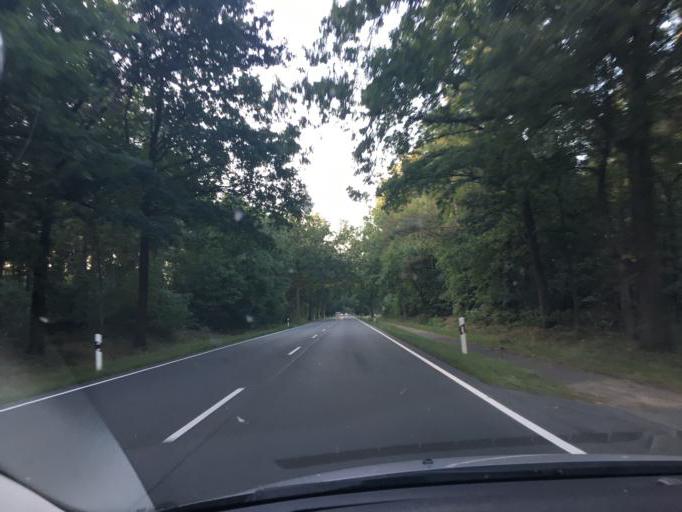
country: DE
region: Lower Saxony
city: Wietzendorf
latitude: 52.9057
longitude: 9.9181
